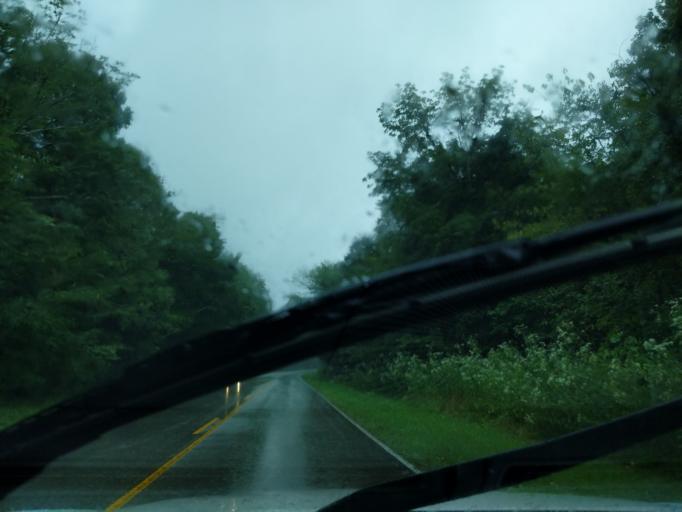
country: US
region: Kentucky
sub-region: Barren County
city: Cave City
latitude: 37.1392
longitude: -86.0802
